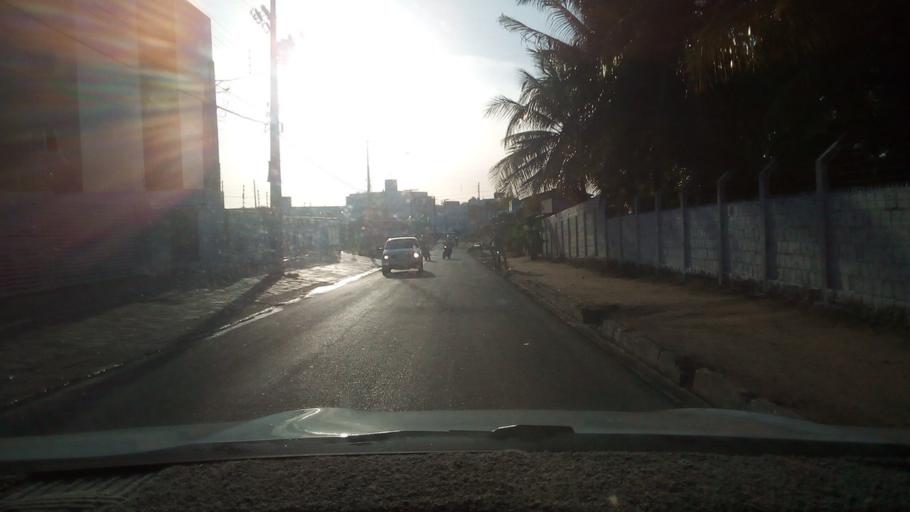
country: BR
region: Paraiba
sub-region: Conde
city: Conde
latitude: -7.1992
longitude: -34.8617
